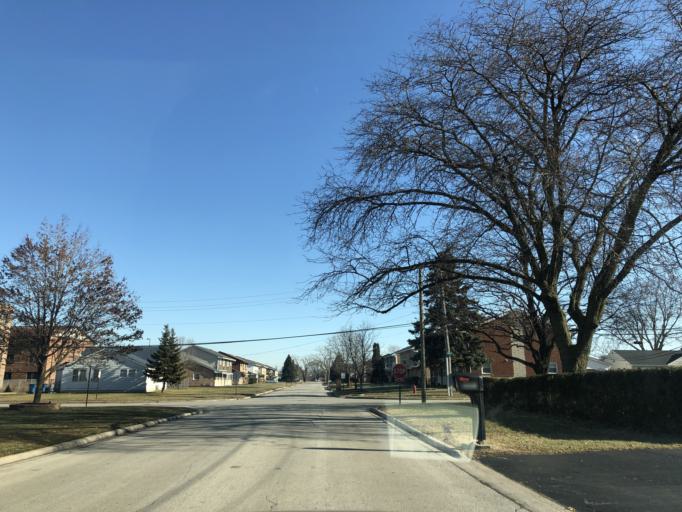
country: US
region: Illinois
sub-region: Cook County
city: Bridgeview
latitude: 41.7461
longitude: -87.8052
